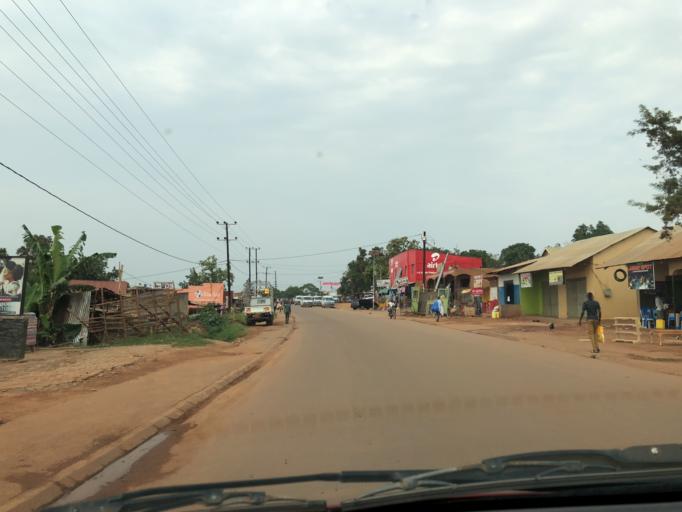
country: UG
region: Central Region
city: Kampala Central Division
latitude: 0.3941
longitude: 32.5932
